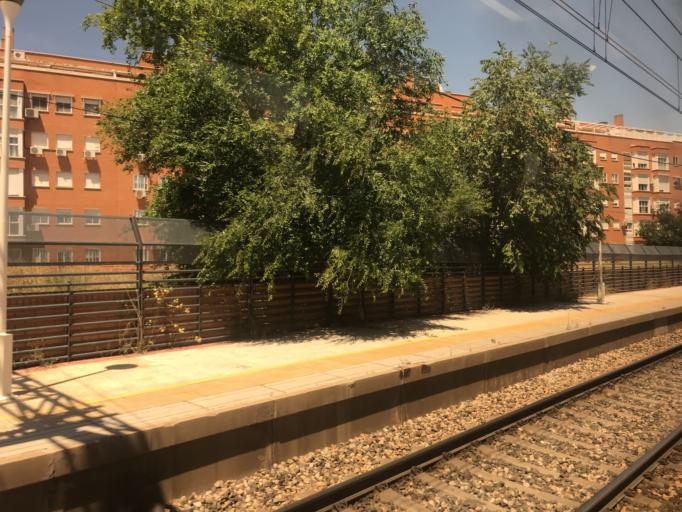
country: ES
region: Madrid
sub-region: Provincia de Madrid
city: Villaverde
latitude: 40.3314
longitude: -3.7003
